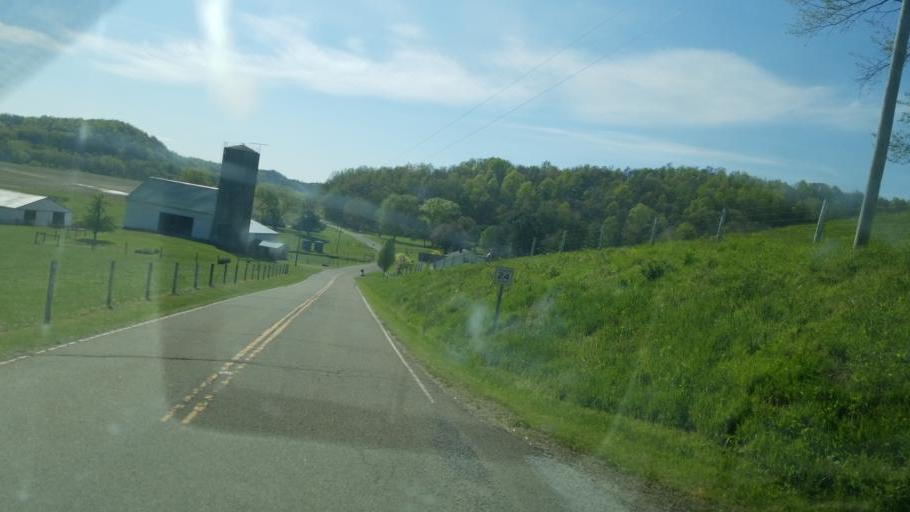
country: US
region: Ohio
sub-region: Coshocton County
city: Coshocton
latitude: 40.3577
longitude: -81.9490
